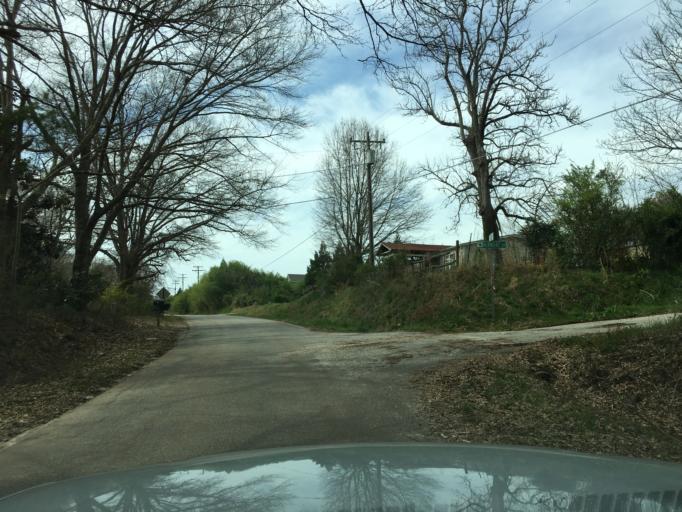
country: US
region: South Carolina
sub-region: Spartanburg County
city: Wellford
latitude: 34.8976
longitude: -82.0617
